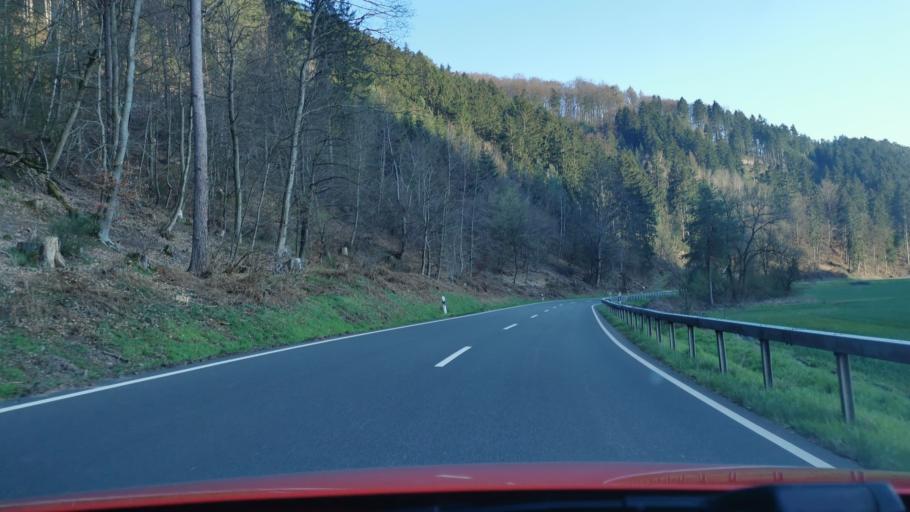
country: DE
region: Rheinland-Pfalz
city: Kordel
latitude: 49.8305
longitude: 6.6533
